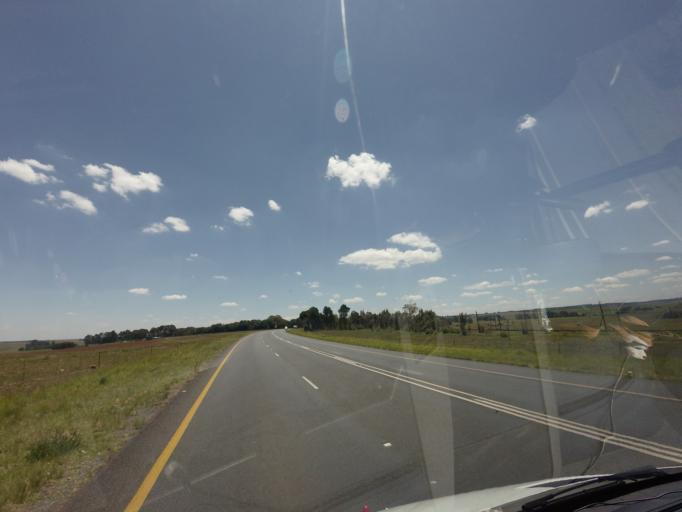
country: ZA
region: Mpumalanga
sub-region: Nkangala District Municipality
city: Belfast
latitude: -25.7340
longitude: 30.1126
